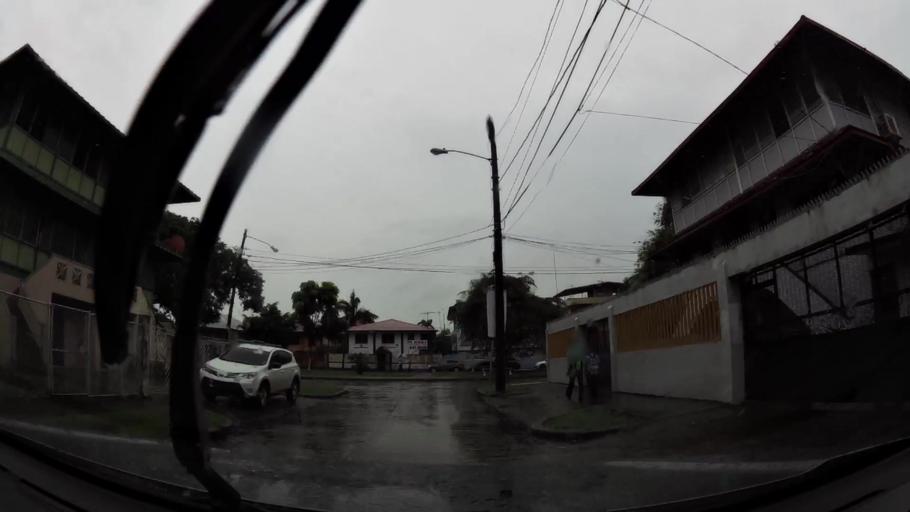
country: PA
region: Colon
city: Colon
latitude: 9.3610
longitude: -79.8991
